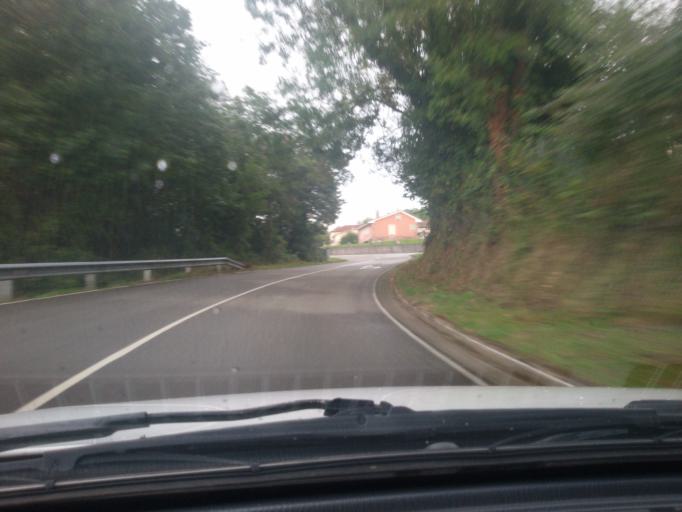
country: ES
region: Asturias
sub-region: Province of Asturias
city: Norena
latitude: 43.3744
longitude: -5.7134
